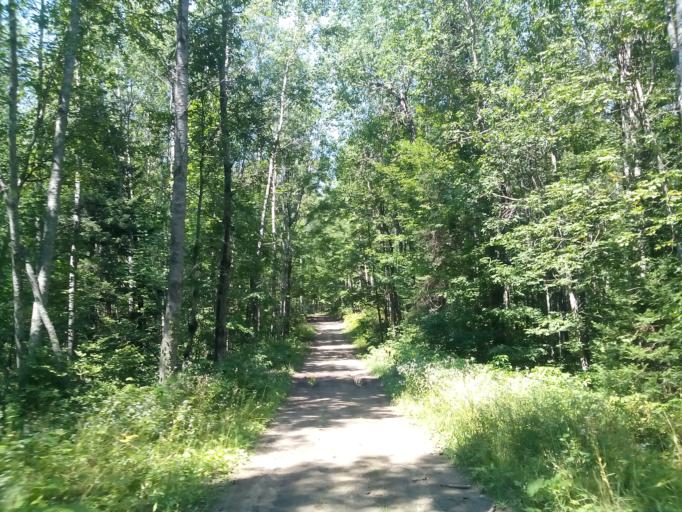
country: US
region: Wisconsin
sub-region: Forest County
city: Crandon
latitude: 45.3631
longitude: -88.5283
